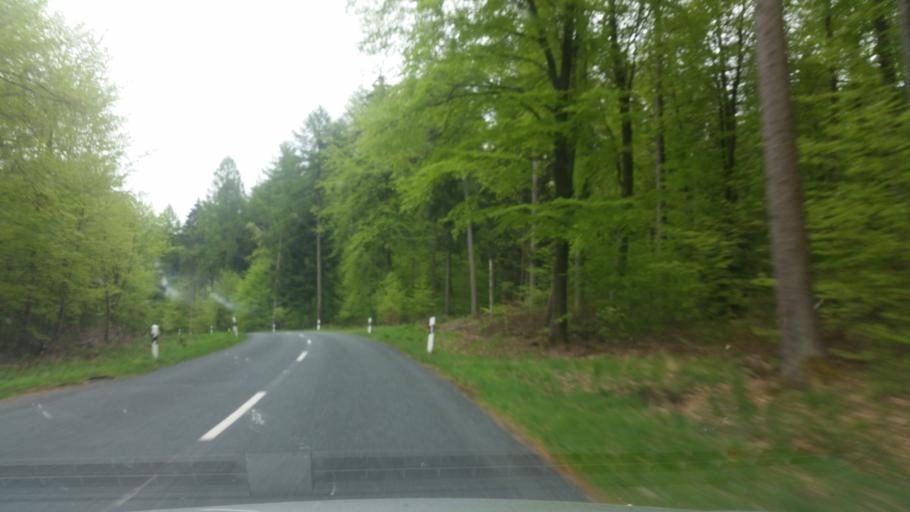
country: DE
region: Lower Saxony
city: Rabke
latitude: 52.1991
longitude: 10.8286
